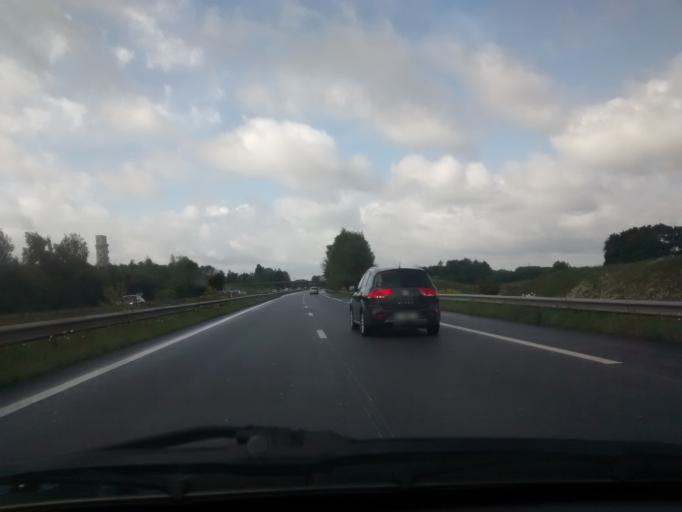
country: FR
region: Brittany
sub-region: Departement d'Ille-et-Vilaine
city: Montgermont
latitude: 48.1282
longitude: -1.7125
